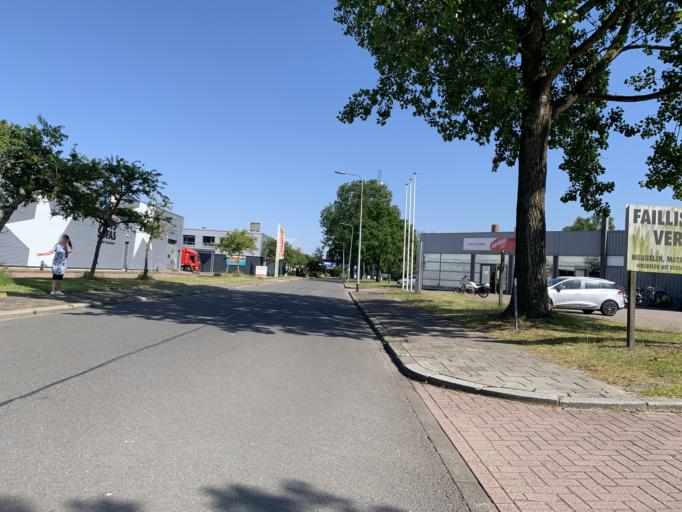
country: NL
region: Groningen
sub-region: Gemeente Groningen
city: Groningen
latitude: 53.2131
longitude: 6.5339
